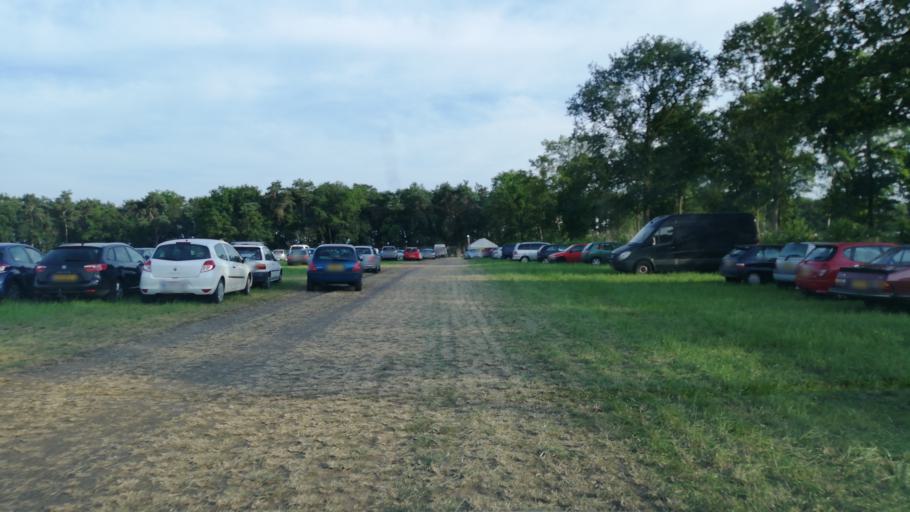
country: NL
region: Overijssel
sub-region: Gemeente Dalfsen
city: Dalfsen
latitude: 52.5081
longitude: 6.2830
